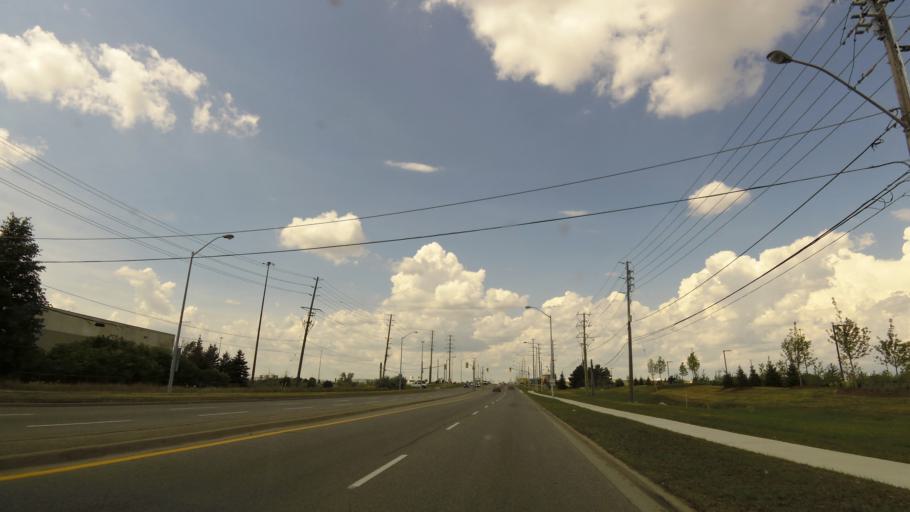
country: CA
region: Ontario
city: Concord
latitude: 43.7784
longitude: -79.5449
